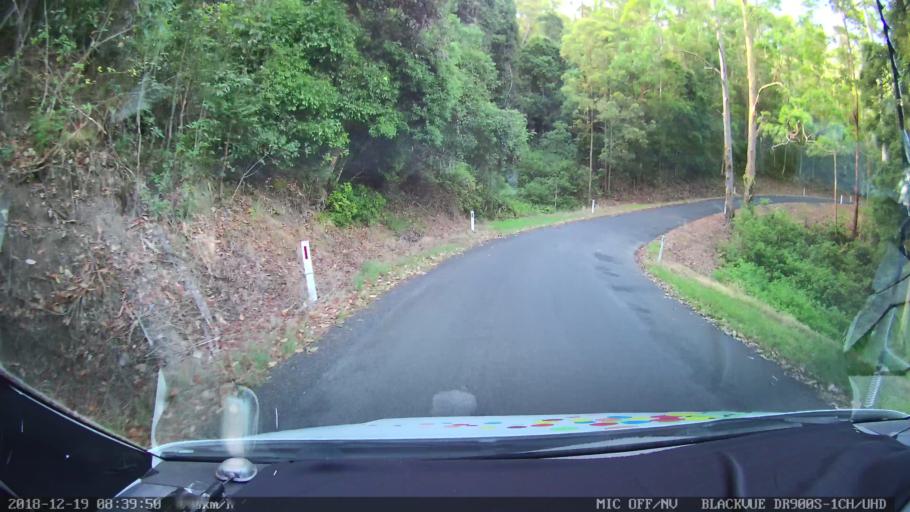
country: AU
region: New South Wales
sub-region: Kyogle
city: Kyogle
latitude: -28.3381
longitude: 152.9714
